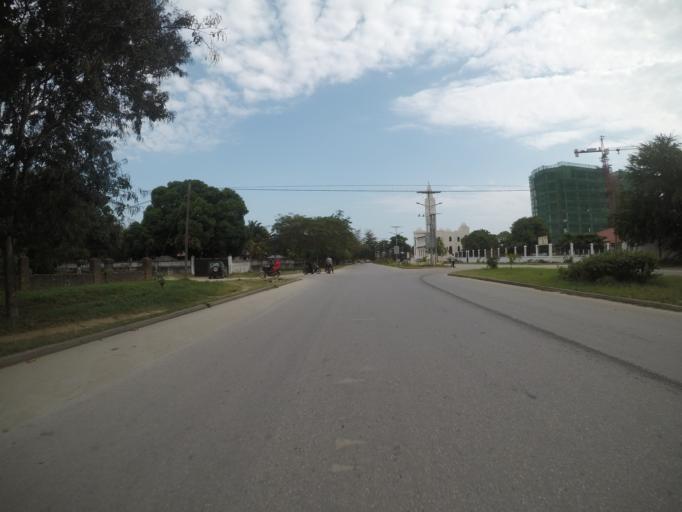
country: TZ
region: Zanzibar Urban/West
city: Zanzibar
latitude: -6.1724
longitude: 39.1988
